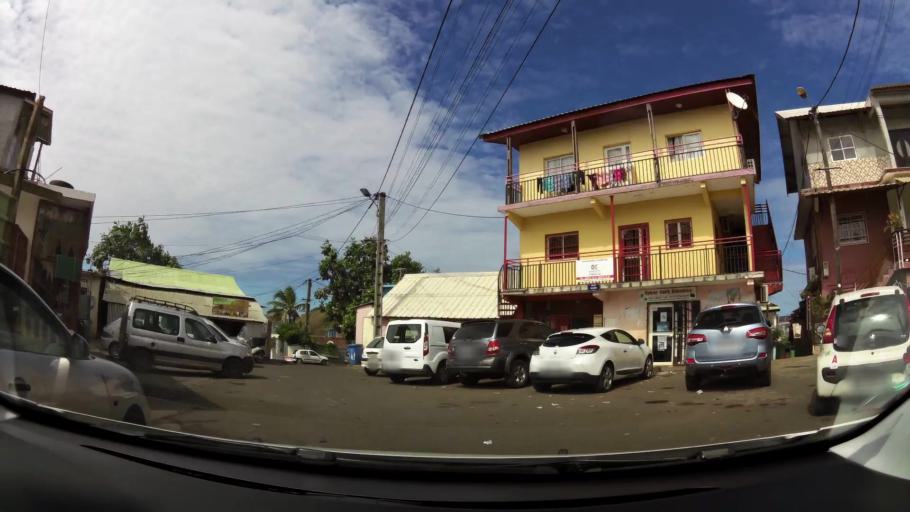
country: YT
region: Mamoudzou
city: Mamoudzou
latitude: -12.7810
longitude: 45.2304
